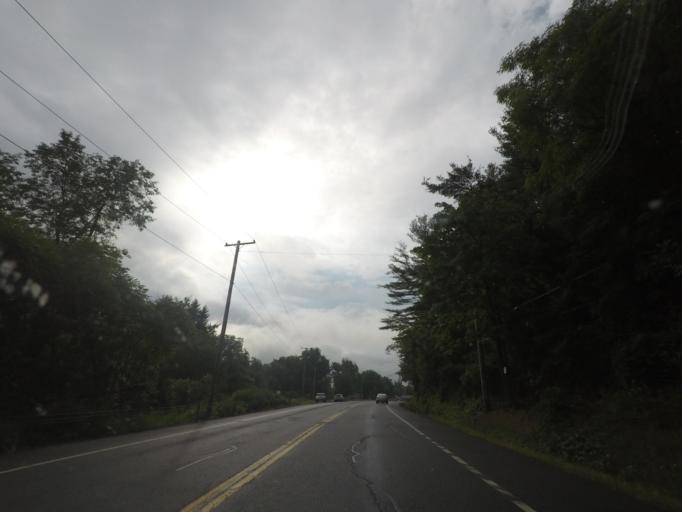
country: US
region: New York
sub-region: Rensselaer County
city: Nassau
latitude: 42.5099
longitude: -73.5657
